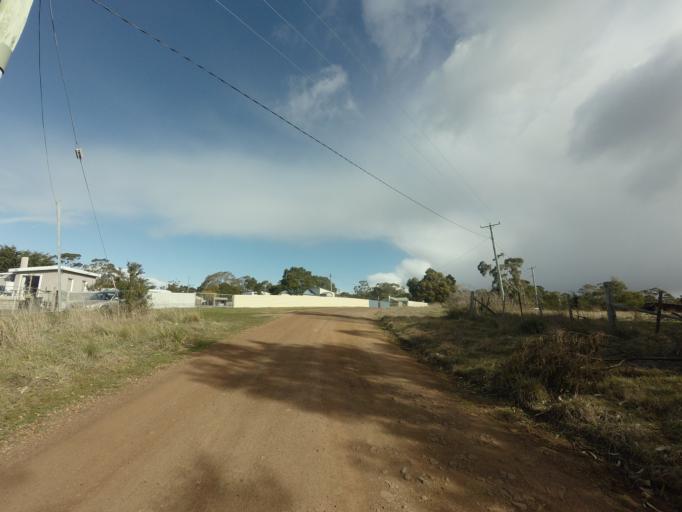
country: AU
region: Tasmania
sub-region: Sorell
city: Sorell
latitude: -42.3250
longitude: 147.9639
